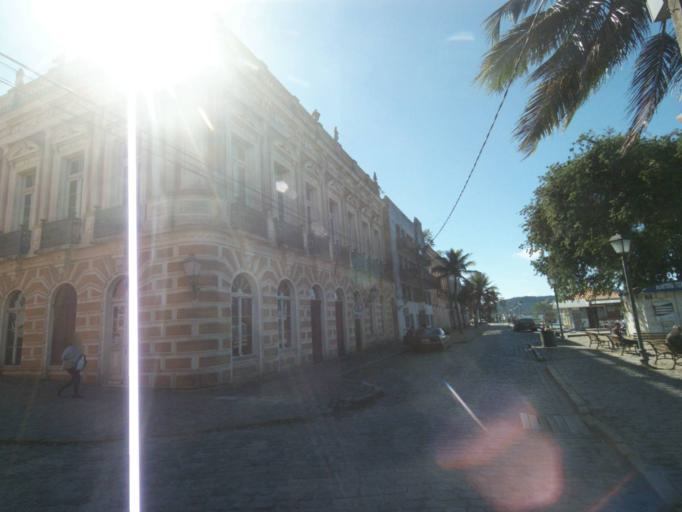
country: BR
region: Parana
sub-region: Paranagua
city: Paranagua
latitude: -25.5202
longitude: -48.5052
